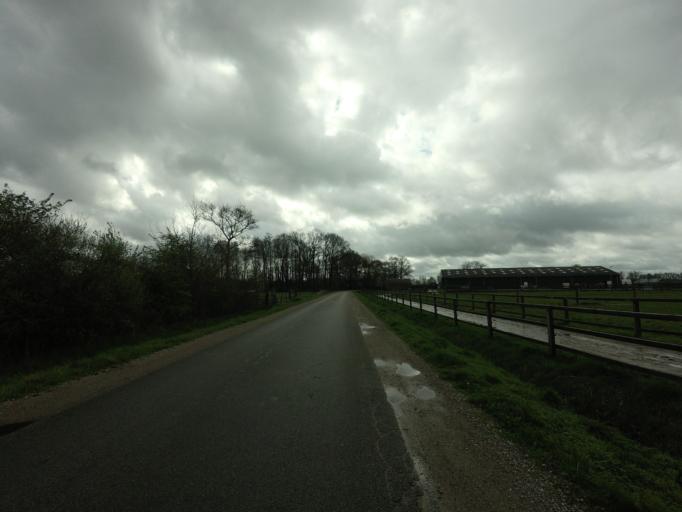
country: NL
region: Gelderland
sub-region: Gemeente Barneveld
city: Stroe
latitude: 52.1790
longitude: 5.6796
